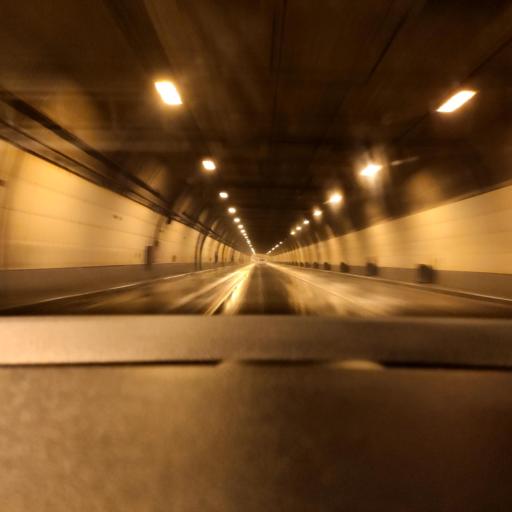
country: RU
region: Moscow
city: Rublevo
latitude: 55.7816
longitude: 37.3939
